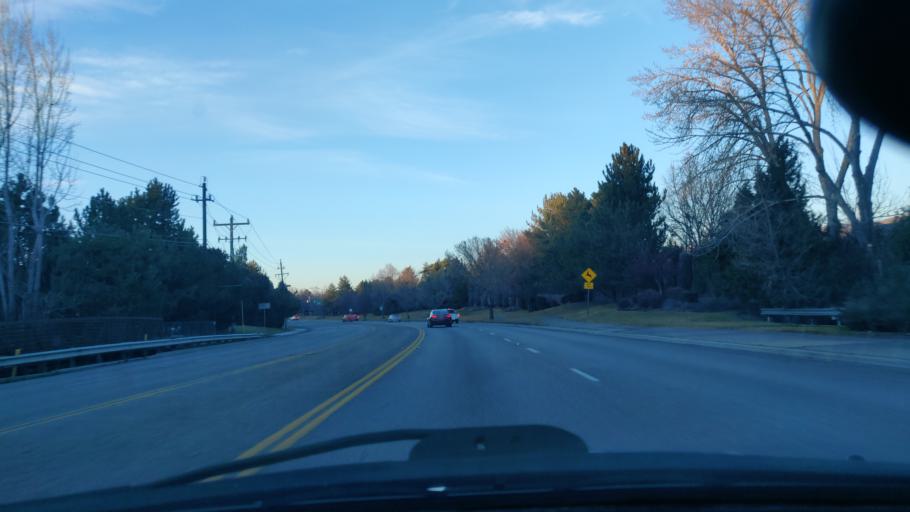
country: US
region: Idaho
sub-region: Ada County
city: Boise
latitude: 43.5871
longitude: -116.1734
